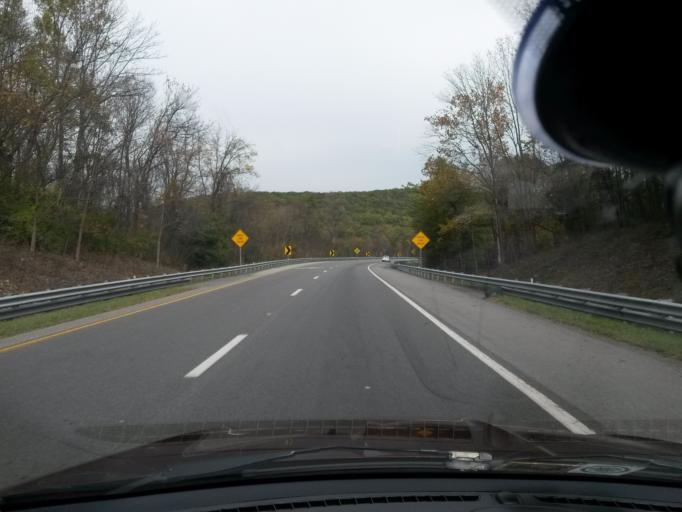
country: US
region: Virginia
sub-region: Roanoke County
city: Hollins
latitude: 37.3397
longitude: -79.9951
